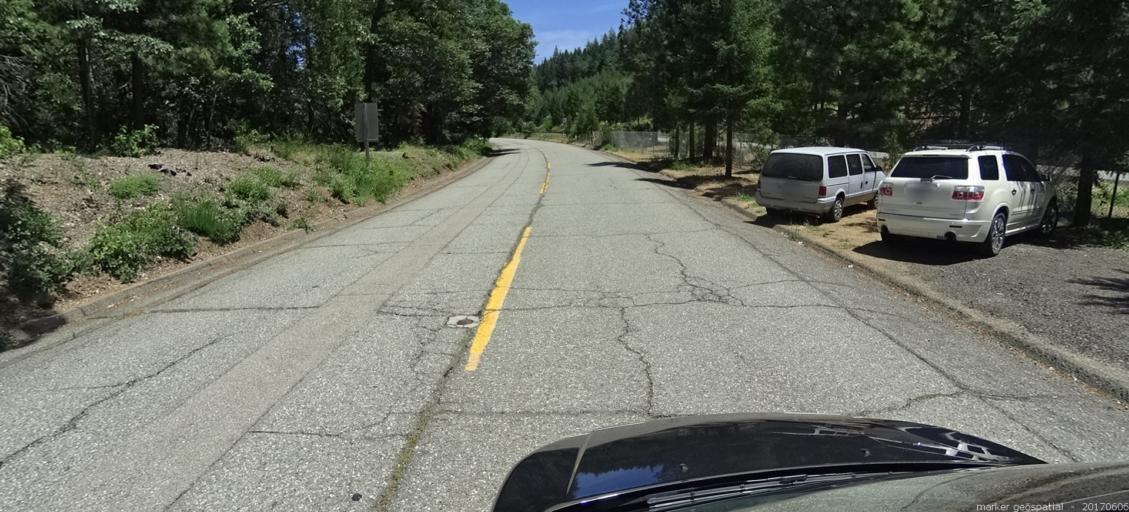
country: US
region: California
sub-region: Siskiyou County
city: Dunsmuir
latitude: 41.2364
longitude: -122.2695
